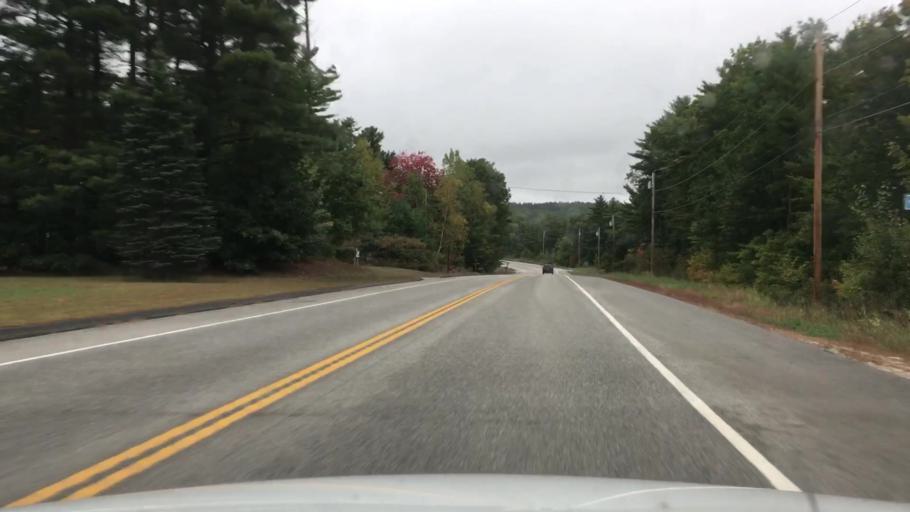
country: US
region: Maine
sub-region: Androscoggin County
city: Poland
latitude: 44.0496
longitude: -70.3802
